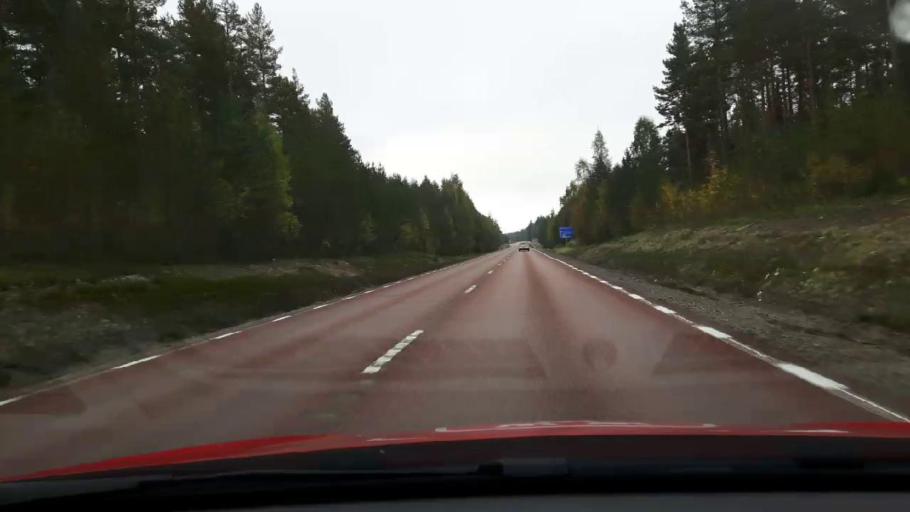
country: SE
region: Gaevleborg
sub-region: Ljusdals Kommun
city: Farila
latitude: 61.8119
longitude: 15.7688
